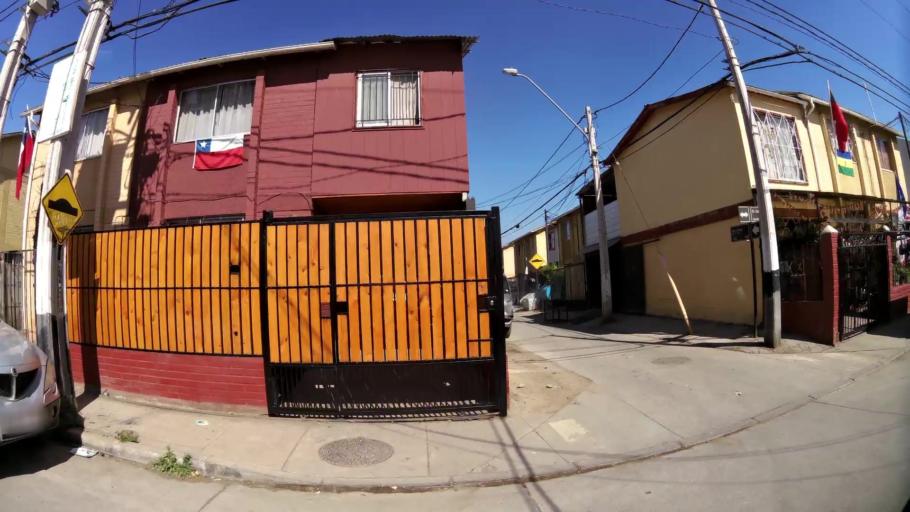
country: CL
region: Santiago Metropolitan
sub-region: Provincia de Santiago
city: Lo Prado
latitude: -33.3522
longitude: -70.7526
